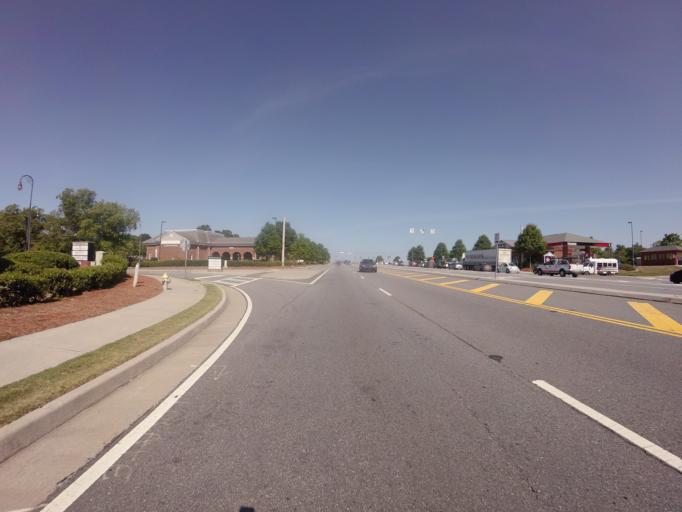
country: US
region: Georgia
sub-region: Fulton County
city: Johns Creek
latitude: 34.0672
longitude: -84.1661
